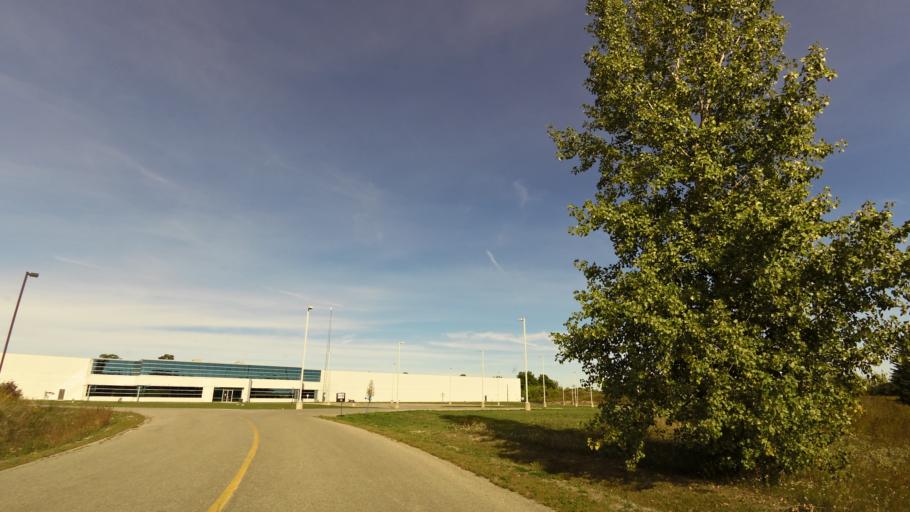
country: CA
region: Ontario
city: Ancaster
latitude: 43.0267
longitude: -79.9981
